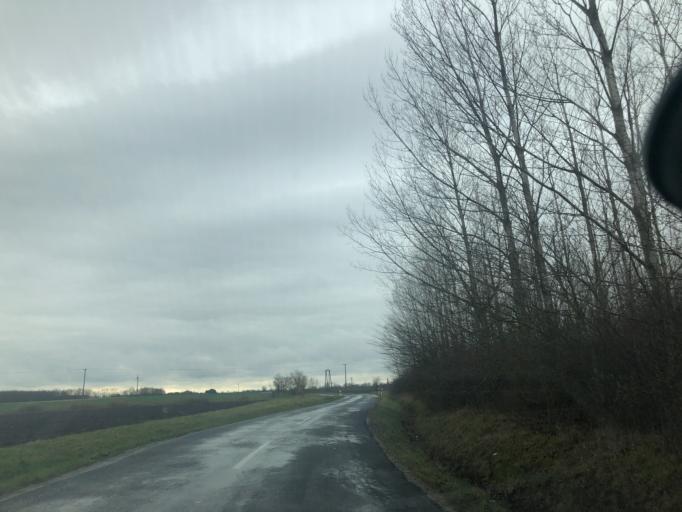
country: HU
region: Gyor-Moson-Sopron
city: Fertoszentmiklos
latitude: 47.6058
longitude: 16.9326
